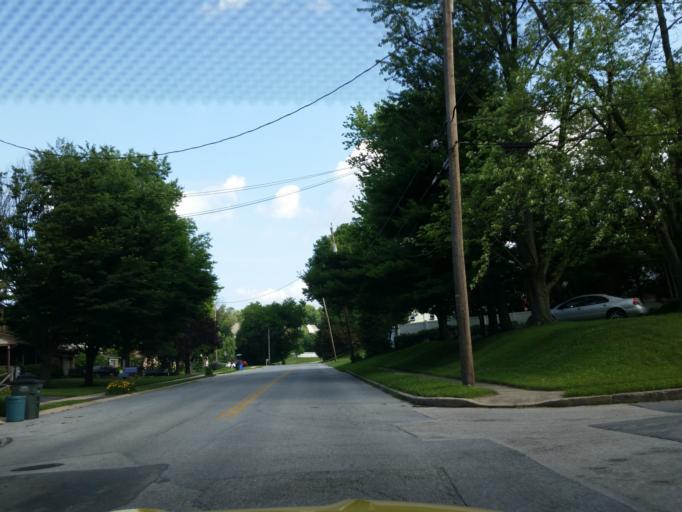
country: US
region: Pennsylvania
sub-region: York County
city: Stonybrook
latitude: 39.9817
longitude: -76.6238
